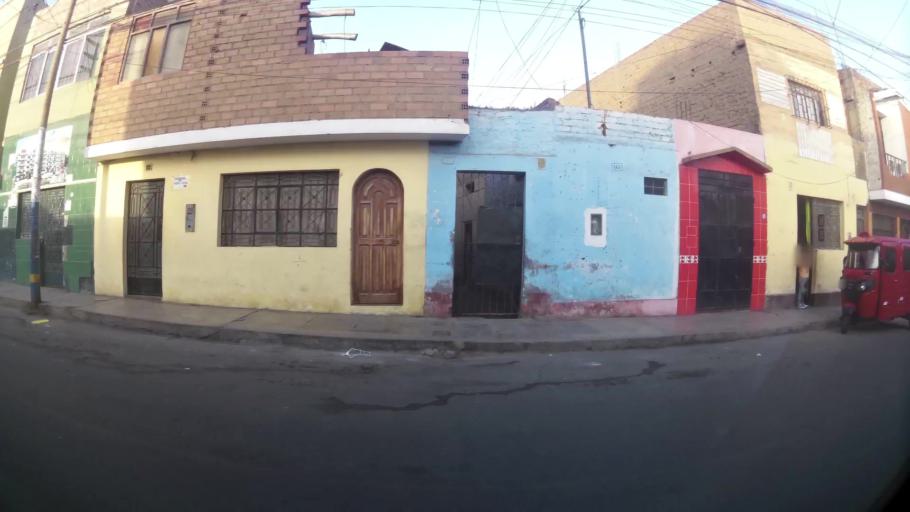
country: PE
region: Lima
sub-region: Huaura
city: Huacho
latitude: -11.1044
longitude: -77.6110
